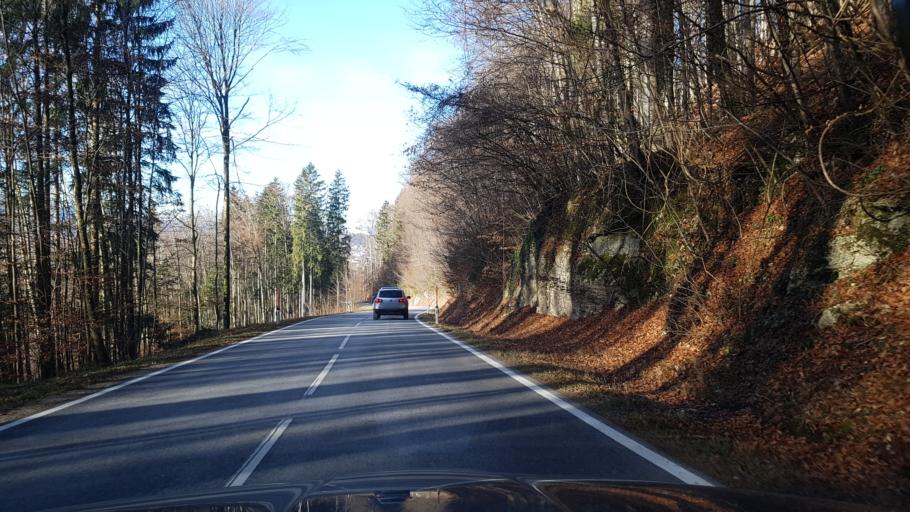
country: AT
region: Salzburg
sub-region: Politischer Bezirk Salzburg-Umgebung
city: Elsbethen
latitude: 47.7717
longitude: 13.0965
